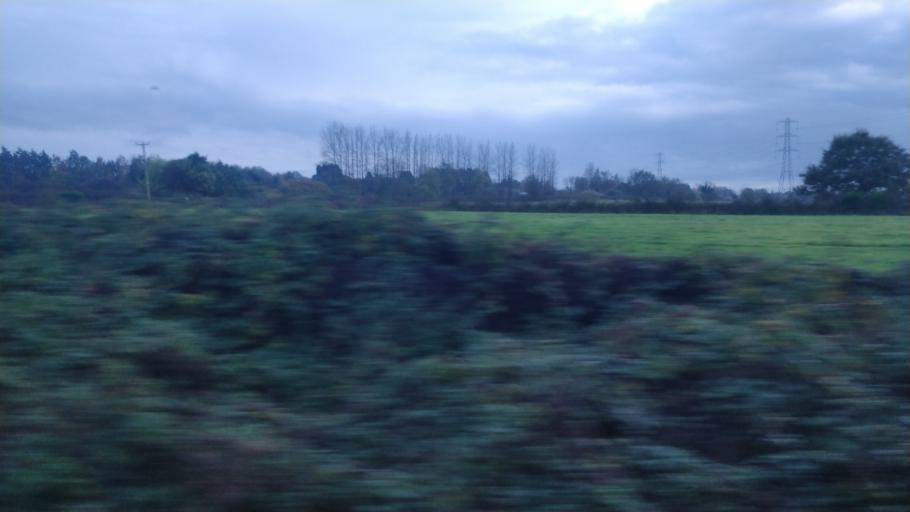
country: GB
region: England
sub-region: Lancashire
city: Parbold
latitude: 53.5957
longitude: -2.7949
